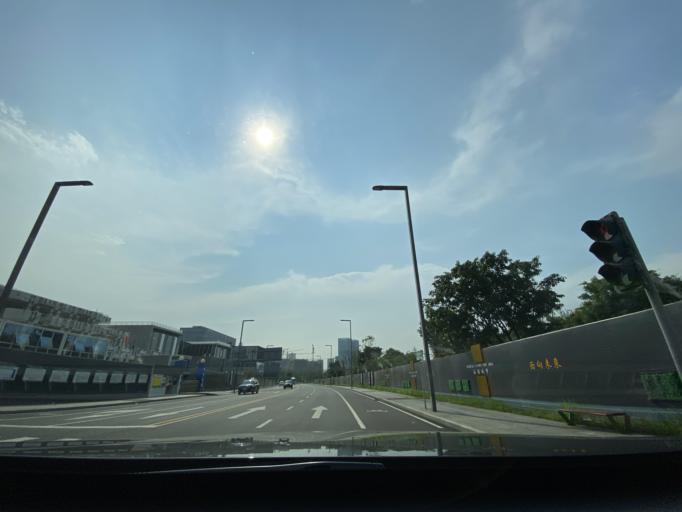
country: CN
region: Sichuan
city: Dongsheng
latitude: 30.3932
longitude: 104.0818
